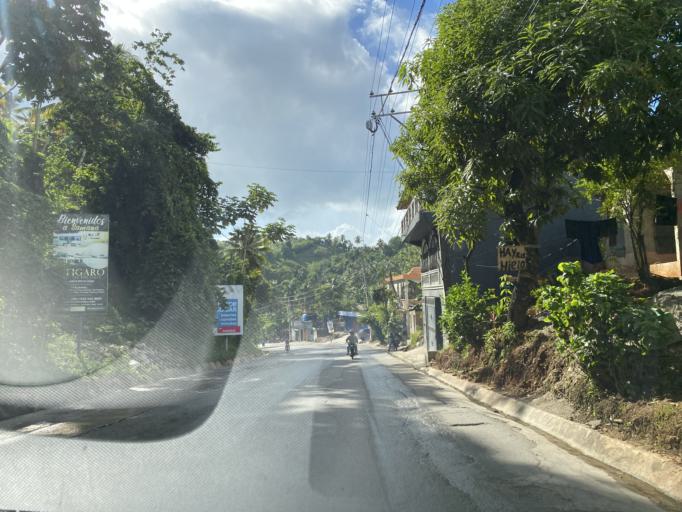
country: DO
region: Samana
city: Samana
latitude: 19.2096
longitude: -69.3551
